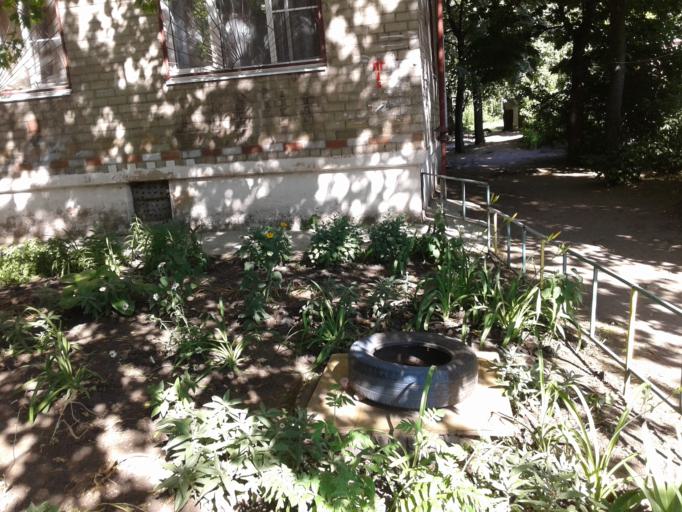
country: RU
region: Voronezj
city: Voronezh
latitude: 51.6689
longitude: 39.1633
